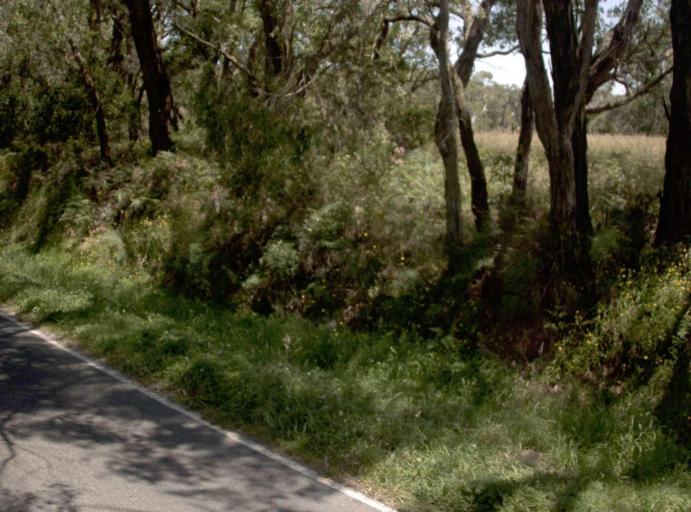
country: AU
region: Victoria
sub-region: Bass Coast
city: North Wonthaggi
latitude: -38.6642
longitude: 145.9280
